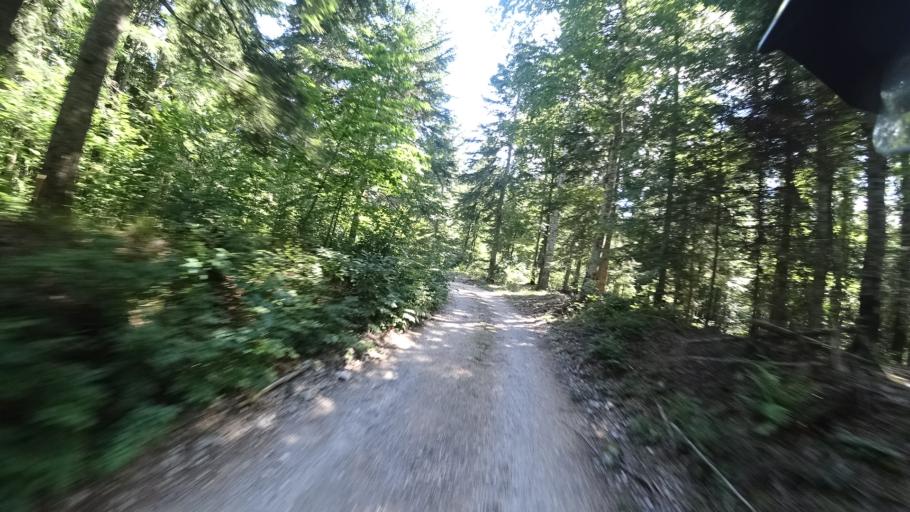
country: BA
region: Federation of Bosnia and Herzegovina
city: Orasac
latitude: 44.5011
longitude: 15.9343
